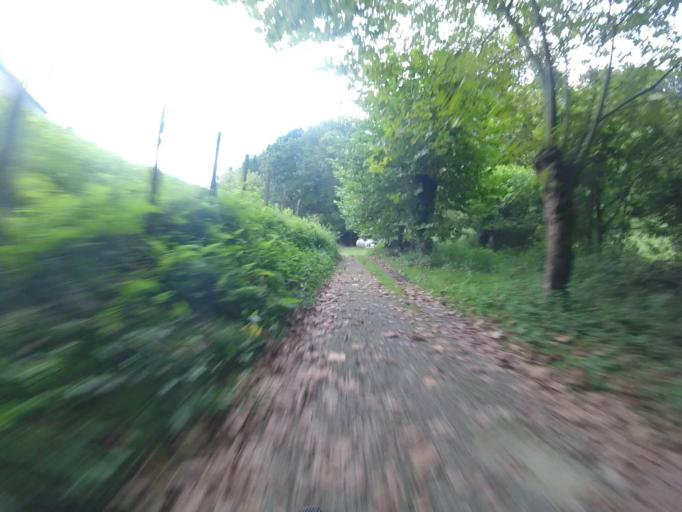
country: ES
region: Basque Country
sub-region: Provincia de Guipuzcoa
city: Errenteria
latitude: 43.2777
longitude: -1.8473
